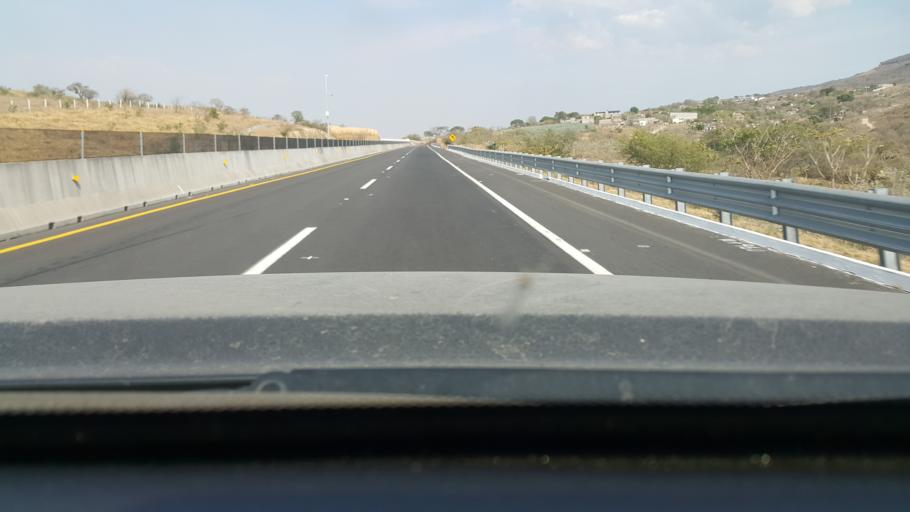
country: MX
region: Nayarit
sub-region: Ahuacatlan
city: Ahuacatlan
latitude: 21.0562
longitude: -104.5253
